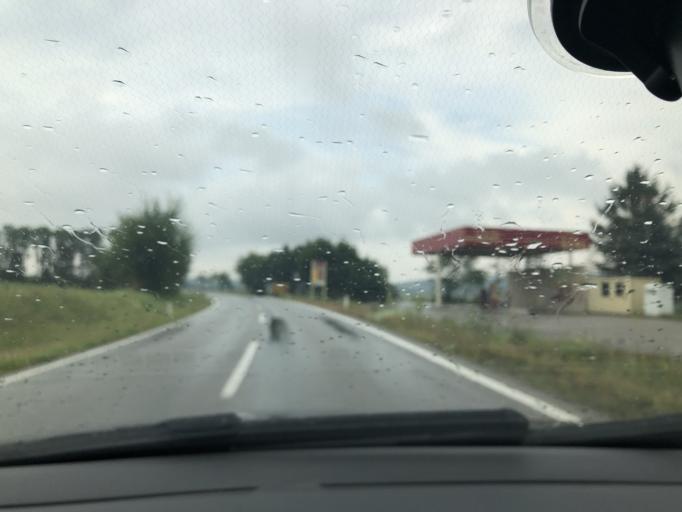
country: AT
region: Lower Austria
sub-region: Politischer Bezirk Ganserndorf
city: Gross-Schweinbarth
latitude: 48.4016
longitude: 16.6452
